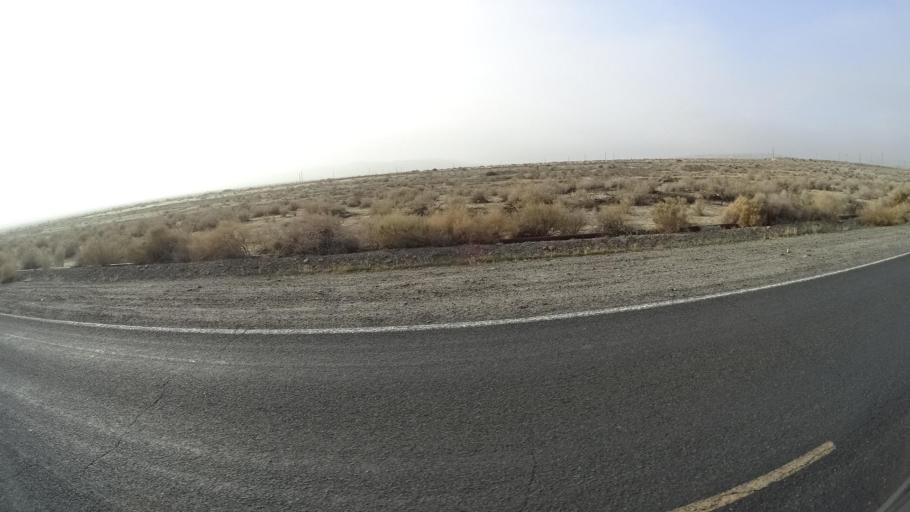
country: US
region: California
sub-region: Kern County
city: Ford City
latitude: 35.2277
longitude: -119.4456
